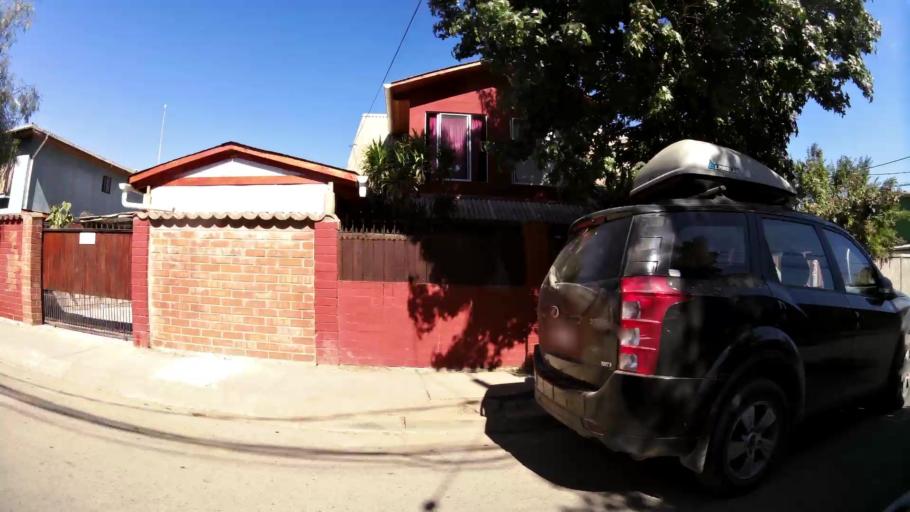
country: CL
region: O'Higgins
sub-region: Provincia de Colchagua
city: Chimbarongo
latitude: -34.5780
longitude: -71.0021
